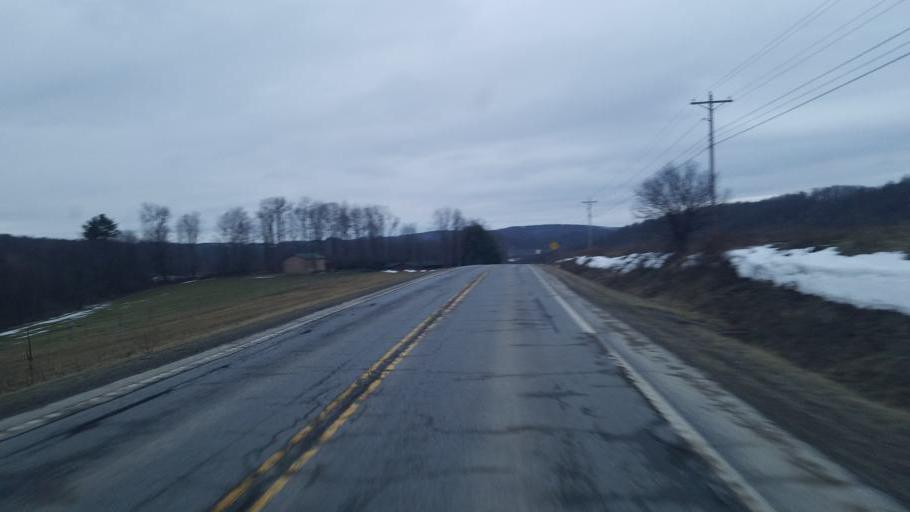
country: US
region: Pennsylvania
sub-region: Potter County
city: Coudersport
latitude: 41.8381
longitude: -77.8949
